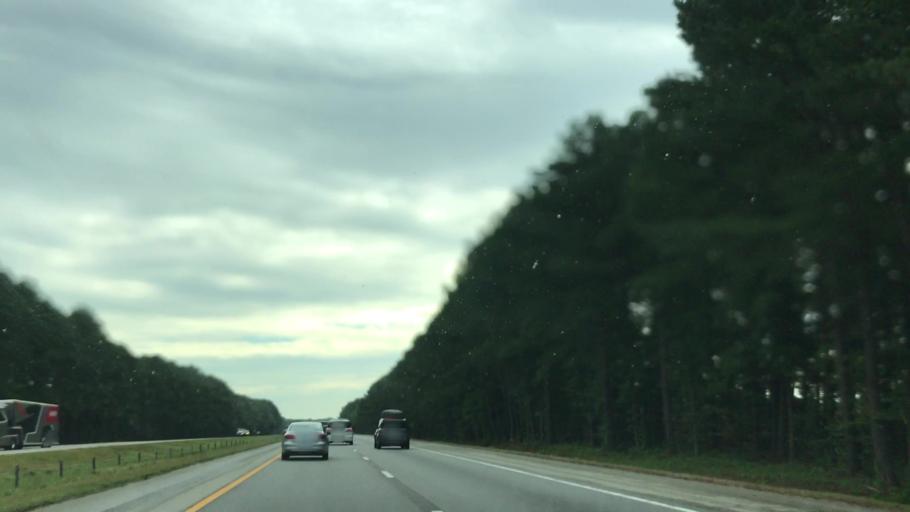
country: US
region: North Carolina
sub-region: Wilson County
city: Lucama
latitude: 35.7218
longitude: -78.0288
